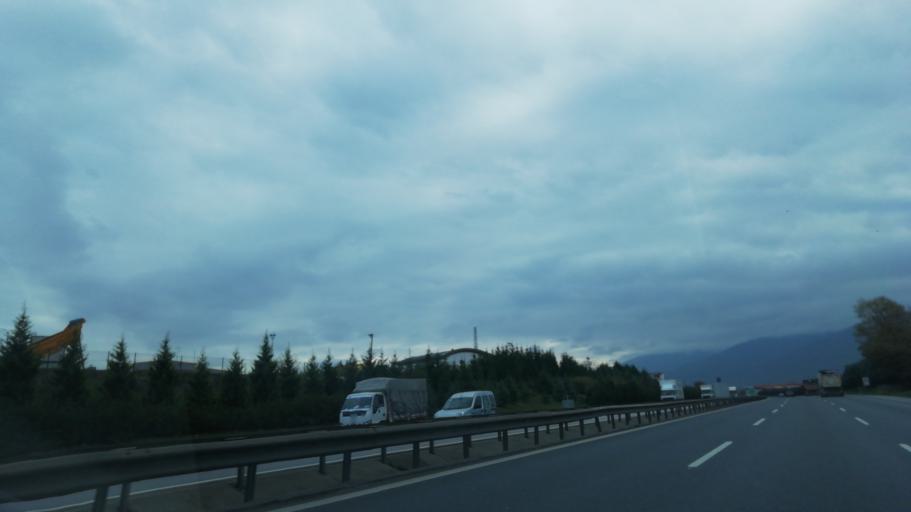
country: TR
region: Kocaeli
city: Kosekoy
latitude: 40.7365
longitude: 30.0496
